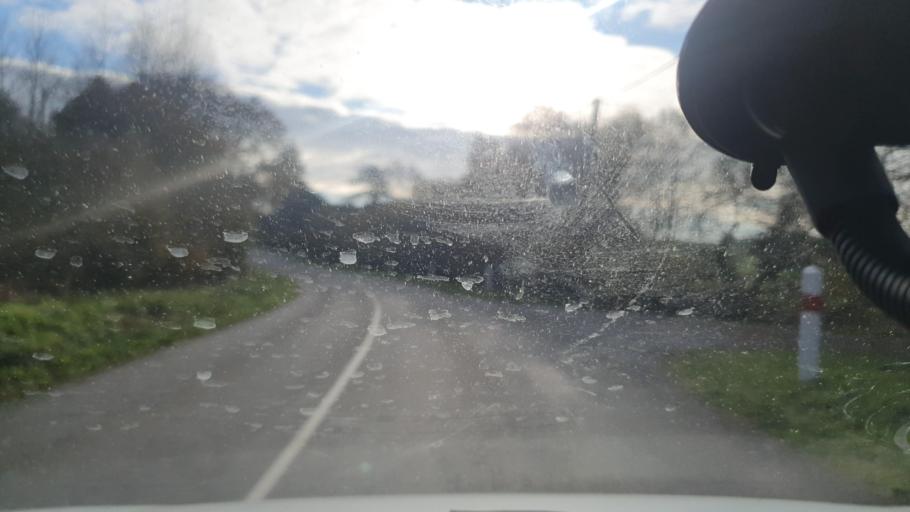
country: FR
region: Brittany
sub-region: Departement du Finistere
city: Briec
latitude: 48.0928
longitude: -4.0034
